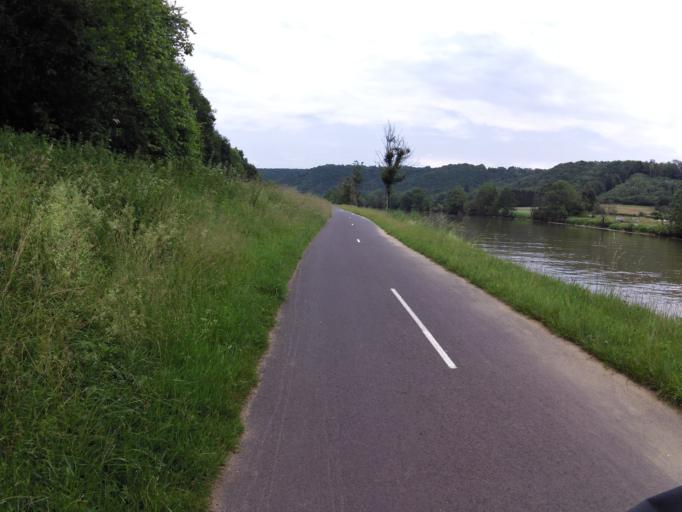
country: FR
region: Champagne-Ardenne
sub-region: Departement des Ardennes
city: Aiglemont
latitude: 49.7845
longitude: 4.7536
